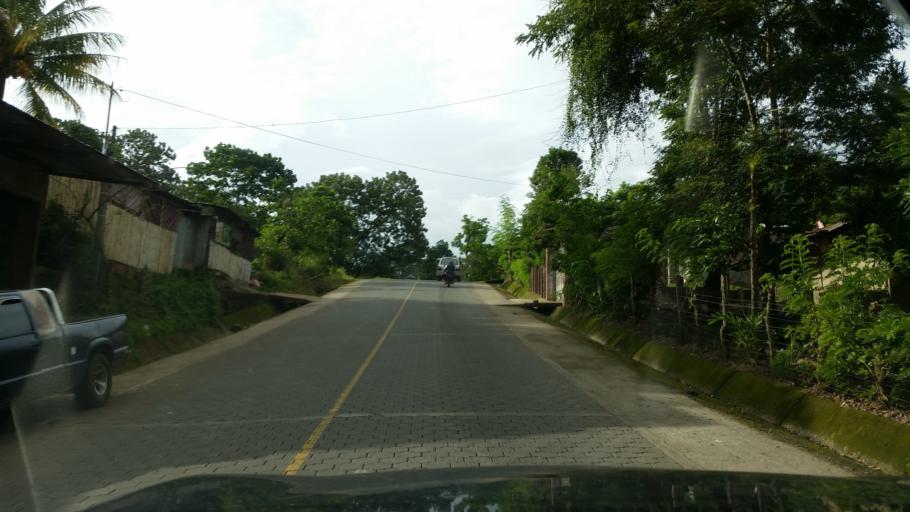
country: NI
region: Matagalpa
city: San Ramon
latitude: 13.1571
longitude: -85.7313
